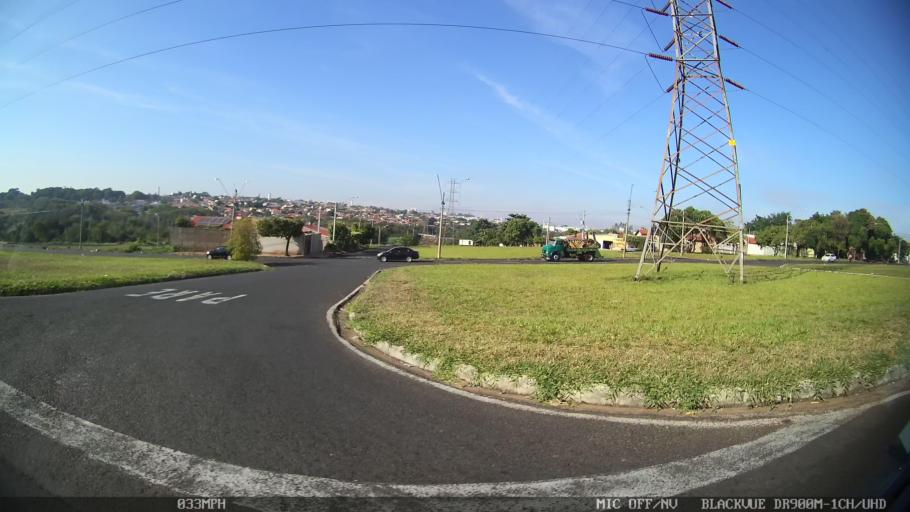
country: BR
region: Sao Paulo
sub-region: Sao Jose Do Rio Preto
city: Sao Jose do Rio Preto
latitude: -20.7646
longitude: -49.3799
